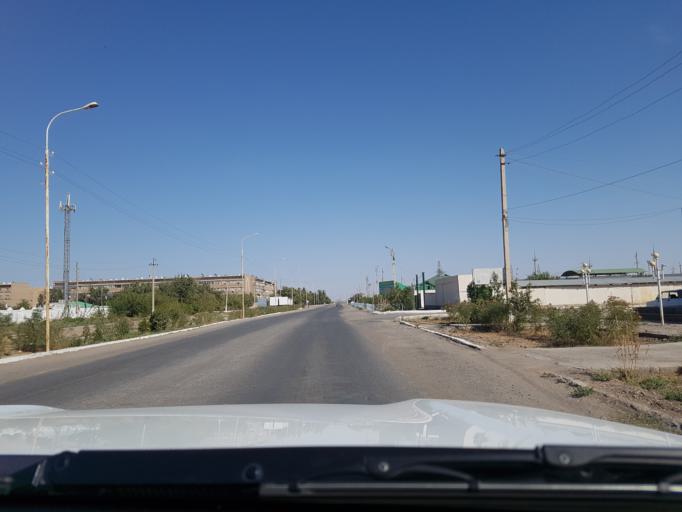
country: IR
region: Razavi Khorasan
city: Sarakhs
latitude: 36.5238
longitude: 61.2217
